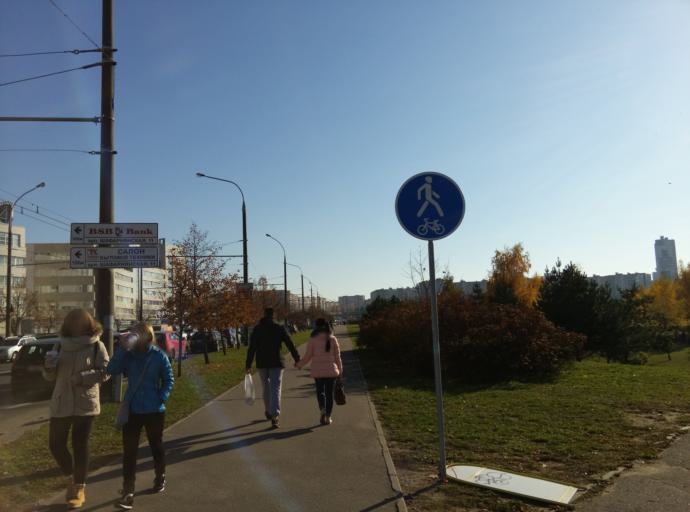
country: BY
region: Minsk
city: Borovlyany
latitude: 53.9469
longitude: 27.6806
